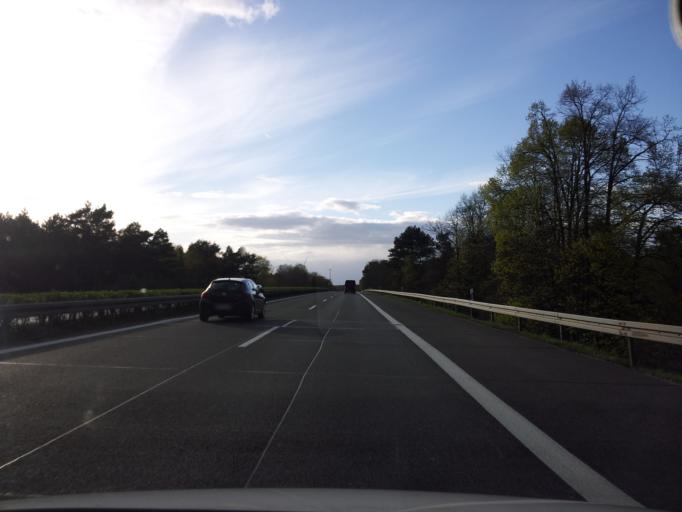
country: DE
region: Brandenburg
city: Werben
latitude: 51.7428
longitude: 14.1545
